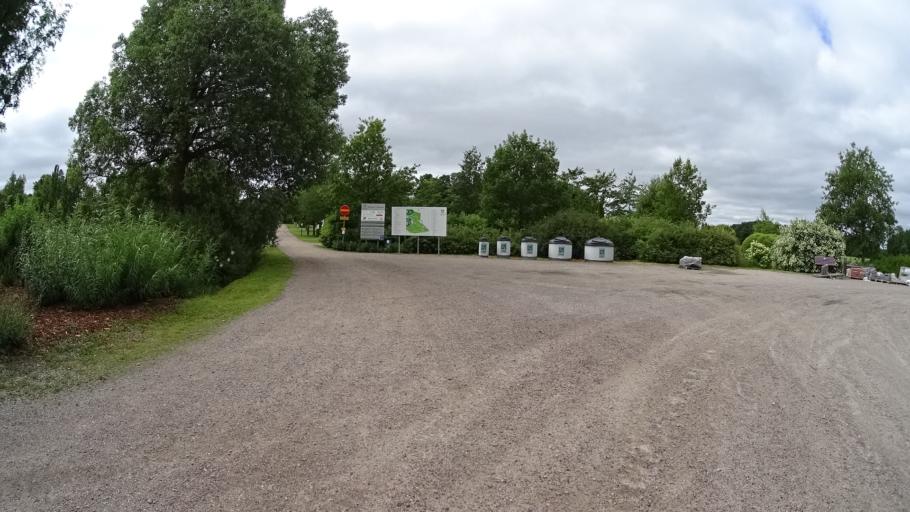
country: FI
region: Uusimaa
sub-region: Helsinki
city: Kauniainen
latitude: 60.2503
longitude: 24.7061
